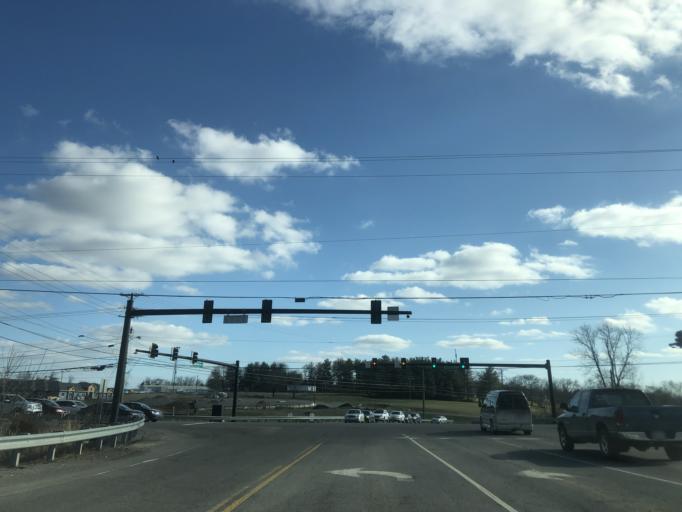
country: US
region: Tennessee
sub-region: Sumner County
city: Gallatin
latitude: 36.3465
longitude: -86.5250
